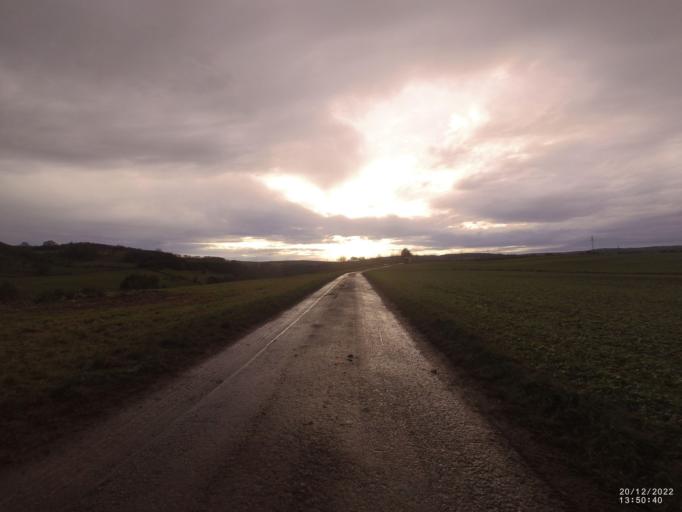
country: DE
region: Rheinland-Pfalz
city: Sinzig
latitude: 50.5340
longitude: 7.2259
